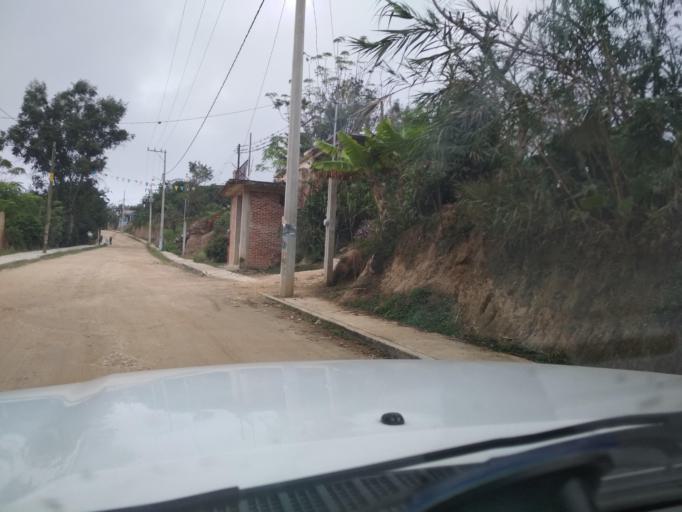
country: MX
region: Veracruz
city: El Castillo
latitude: 19.5446
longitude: -96.8284
